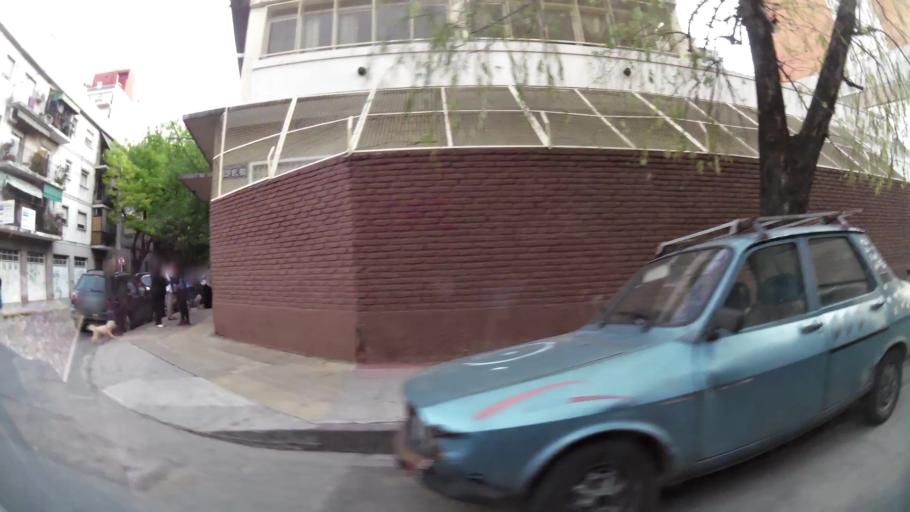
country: AR
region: Buenos Aires F.D.
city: Colegiales
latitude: -34.5489
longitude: -58.4700
